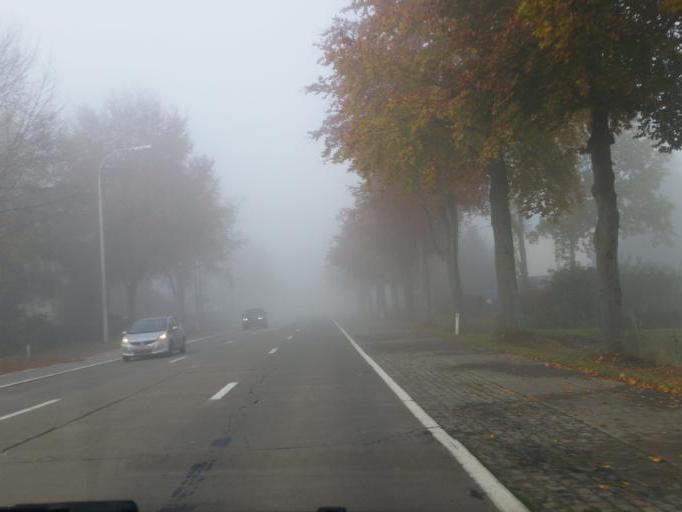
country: BE
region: Flanders
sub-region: Provincie Oost-Vlaanderen
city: Lede
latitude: 50.9499
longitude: 3.9377
